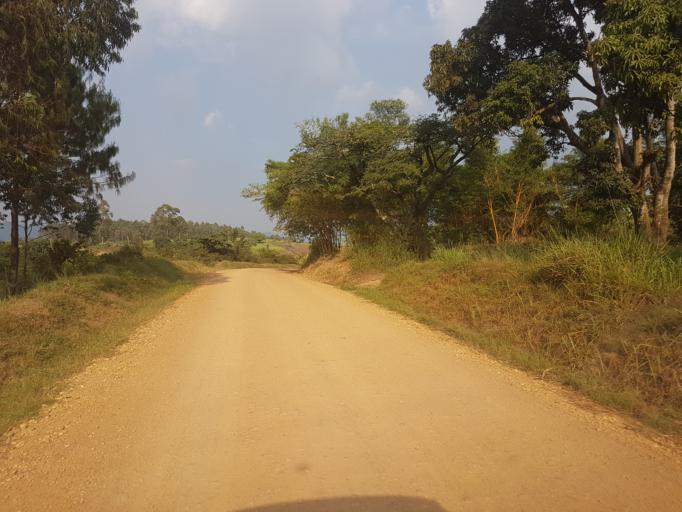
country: UG
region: Western Region
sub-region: Rukungiri District
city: Rukungiri
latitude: -0.6521
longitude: 29.8534
